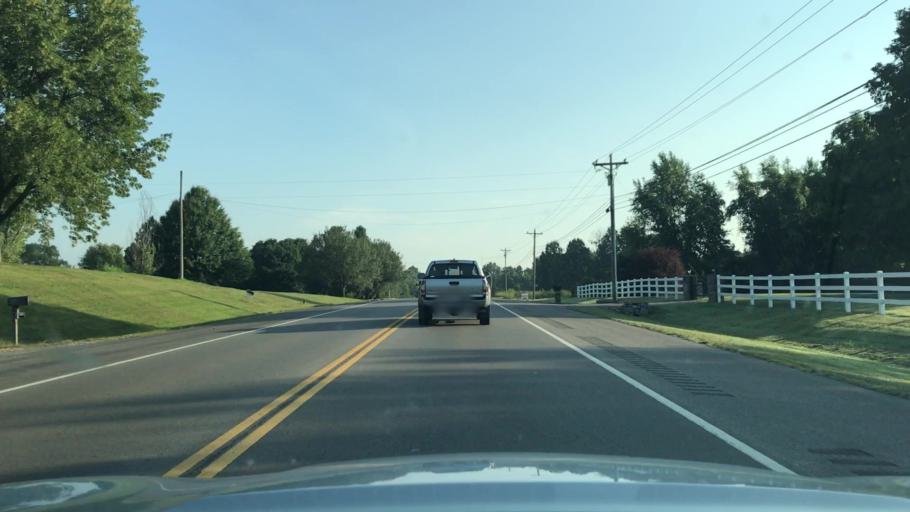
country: US
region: Tennessee
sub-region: Wilson County
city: Rural Hill
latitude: 36.1347
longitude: -86.5191
